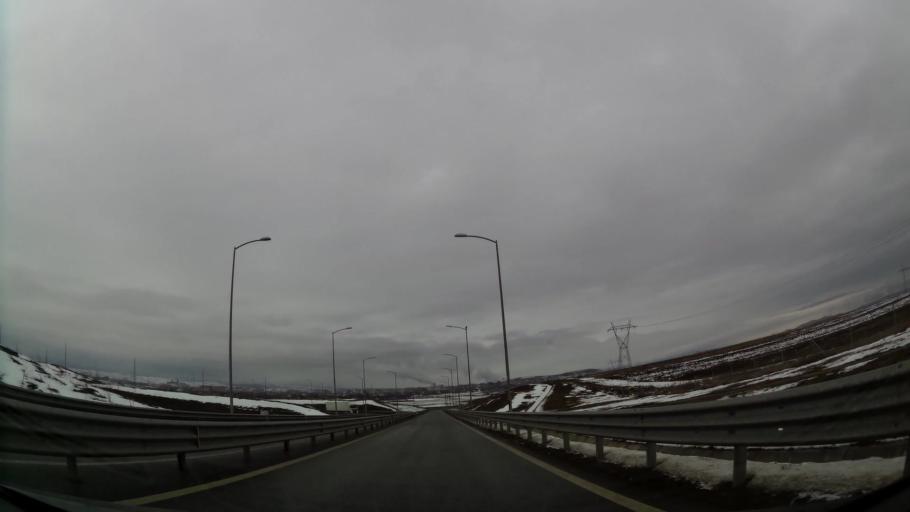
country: XK
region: Pristina
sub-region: Kosovo Polje
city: Kosovo Polje
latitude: 42.6208
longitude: 21.1185
